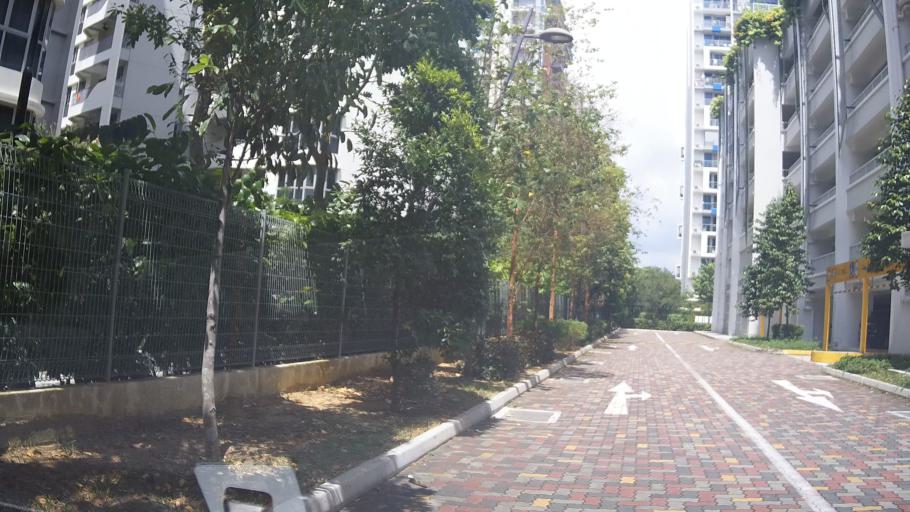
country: SG
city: Singapore
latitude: 1.3508
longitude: 103.9290
